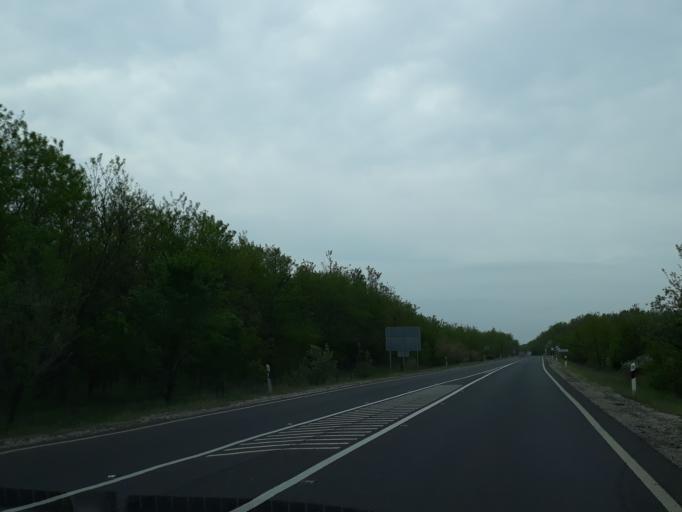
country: HU
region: Szabolcs-Szatmar-Bereg
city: Nyirtass
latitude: 48.1080
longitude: 21.9888
